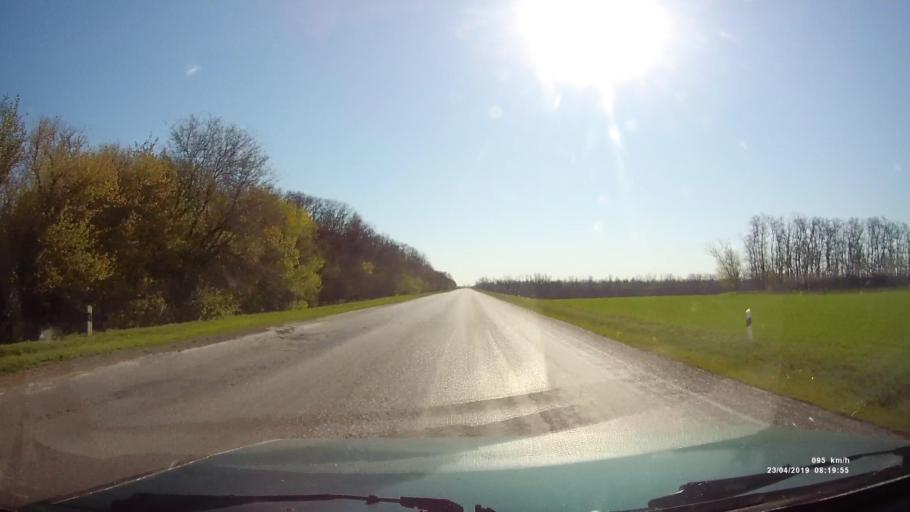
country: RU
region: Rostov
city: Tselina
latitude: 46.5374
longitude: 40.8585
